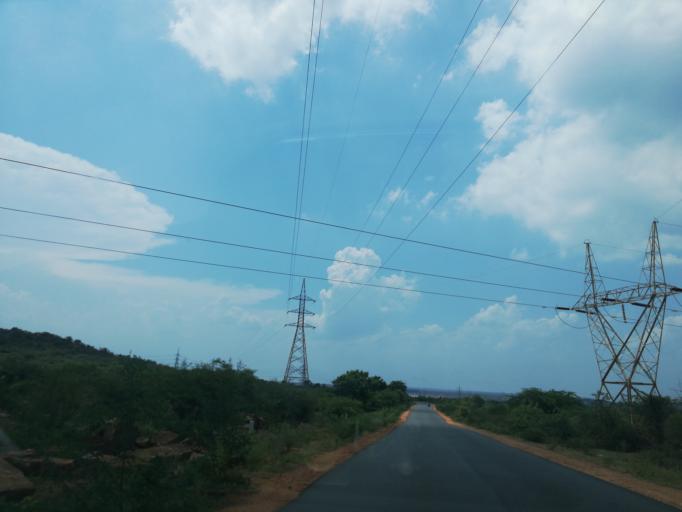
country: IN
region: Andhra Pradesh
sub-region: Guntur
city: Macherla
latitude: 16.5679
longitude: 79.3462
